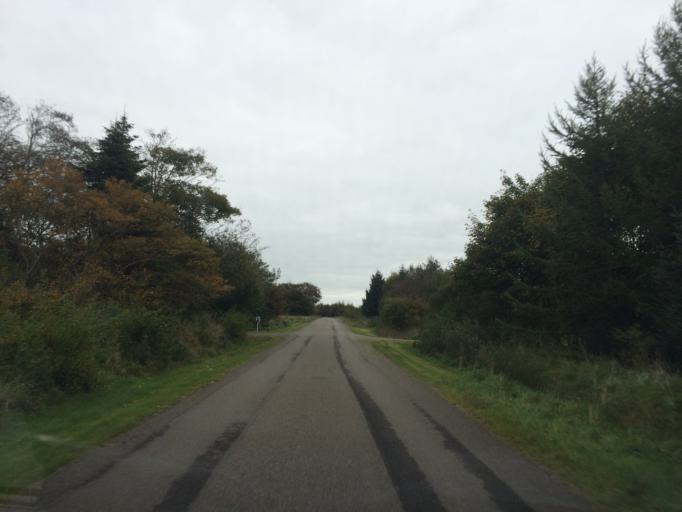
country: DK
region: Central Jutland
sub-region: Holstebro Kommune
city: Ulfborg
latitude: 56.2228
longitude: 8.4381
